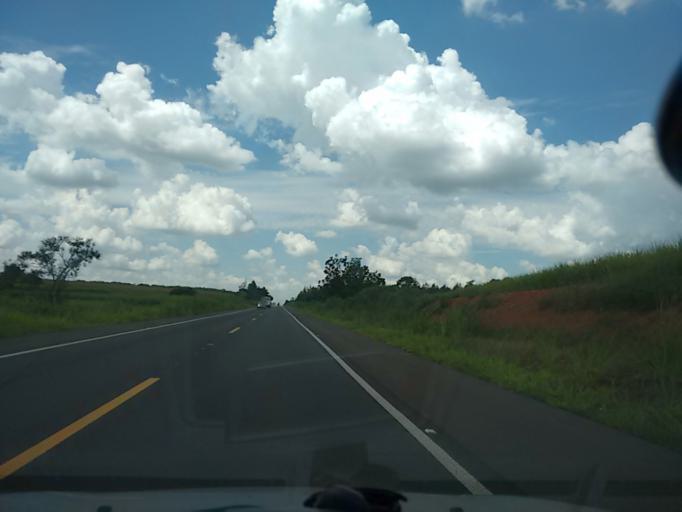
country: BR
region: Sao Paulo
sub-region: Osvaldo Cruz
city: Osvaldo Cruz
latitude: -21.8560
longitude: -50.8417
